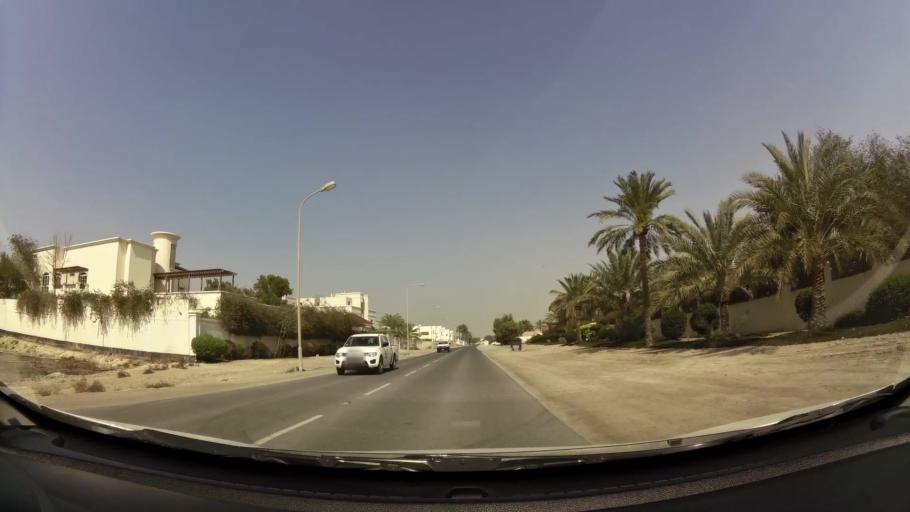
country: BH
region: Northern
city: Madinat `Isa
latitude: 26.1928
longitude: 50.4669
